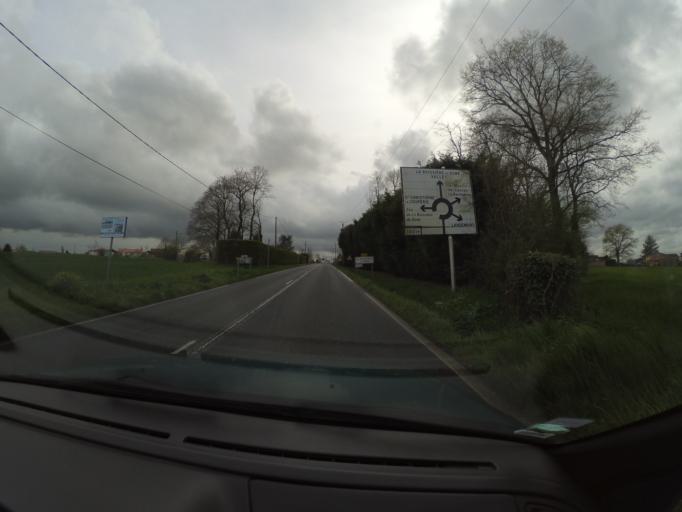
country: FR
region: Pays de la Loire
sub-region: Departement de la Loire-Atlantique
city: La Remaudiere
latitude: 47.2409
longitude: -1.2136
